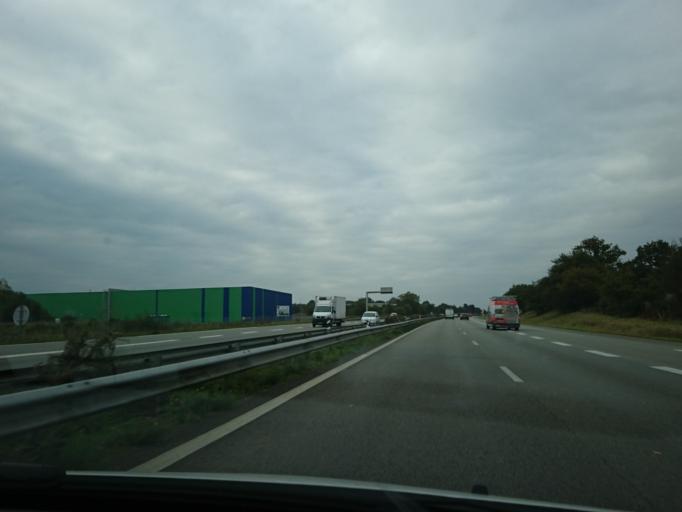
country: FR
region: Pays de la Loire
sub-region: Departement de la Loire-Atlantique
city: Sautron
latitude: 47.2446
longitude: -1.6722
